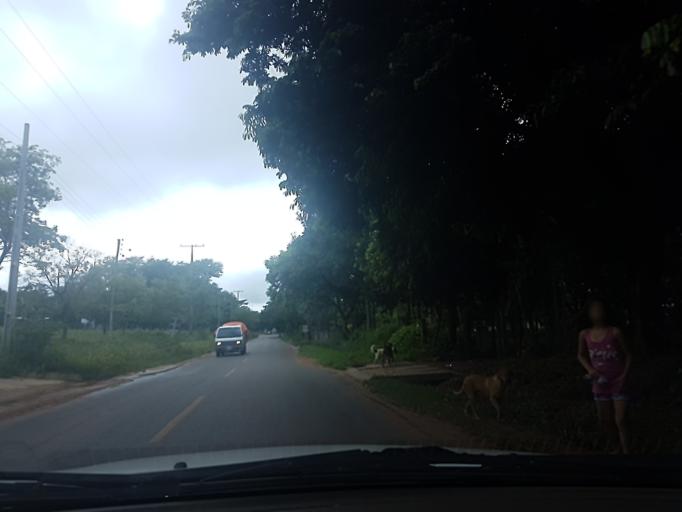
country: PY
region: Central
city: Limpio
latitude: -25.1965
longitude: -57.4574
